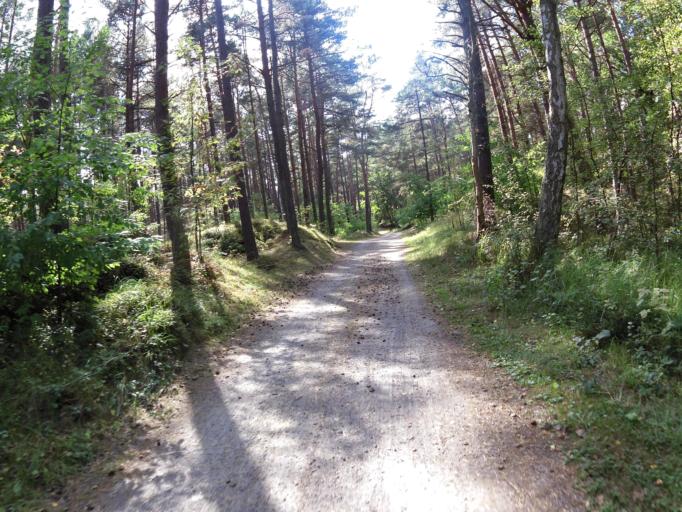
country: DE
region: Mecklenburg-Vorpommern
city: Karlshagen
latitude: 54.1104
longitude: 13.8537
